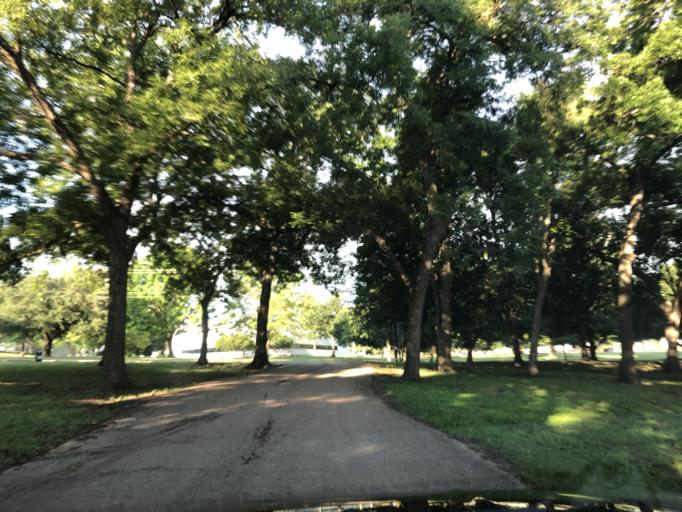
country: US
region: Texas
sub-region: Dallas County
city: Garland
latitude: 32.8486
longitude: -96.6150
